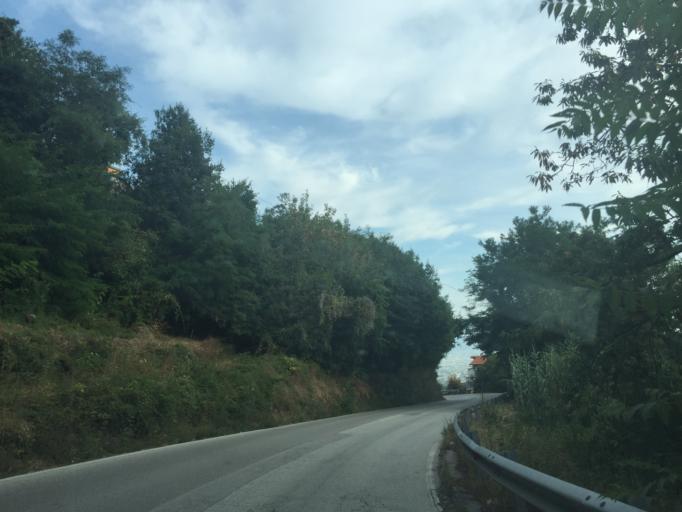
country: IT
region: Tuscany
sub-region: Provincia di Pistoia
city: Campo Tizzoro
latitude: 43.9839
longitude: 10.8611
